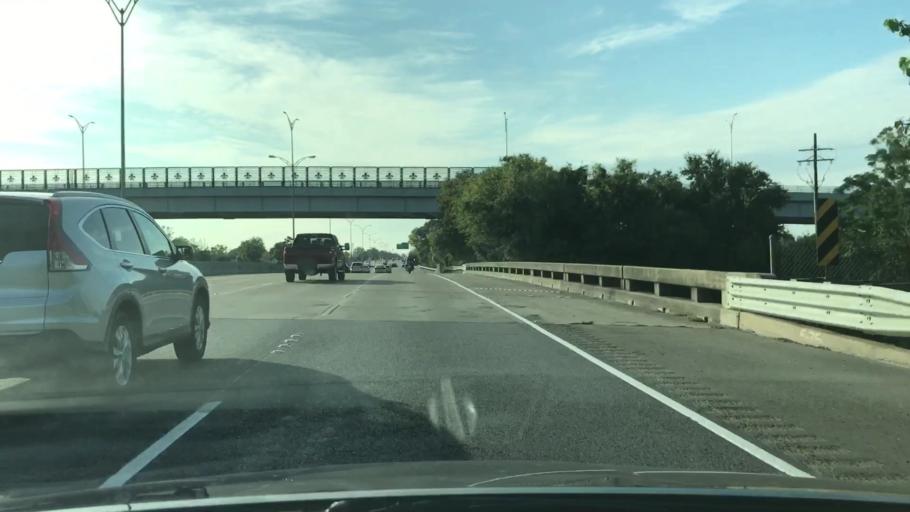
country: US
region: Louisiana
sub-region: Orleans Parish
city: New Orleans
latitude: 29.9931
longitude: -90.0858
